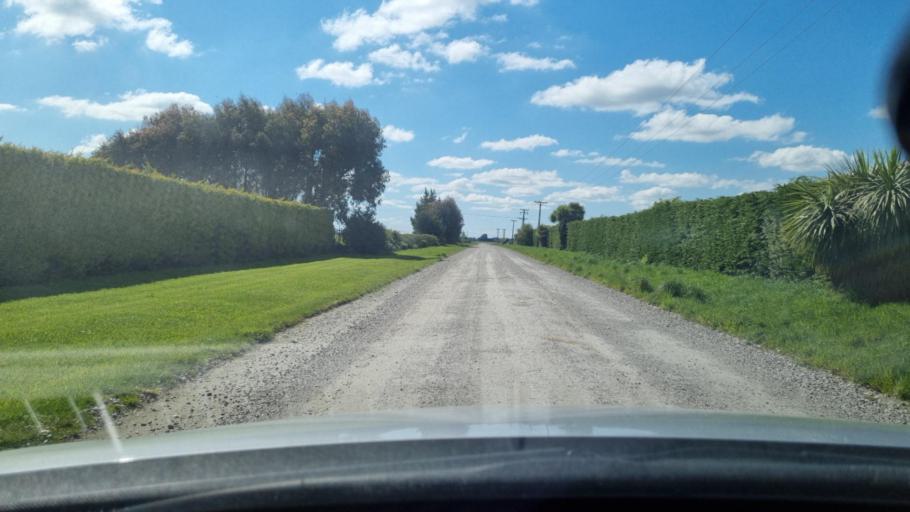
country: NZ
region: Southland
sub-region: Invercargill City
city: Invercargill
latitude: -46.3735
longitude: 168.2985
